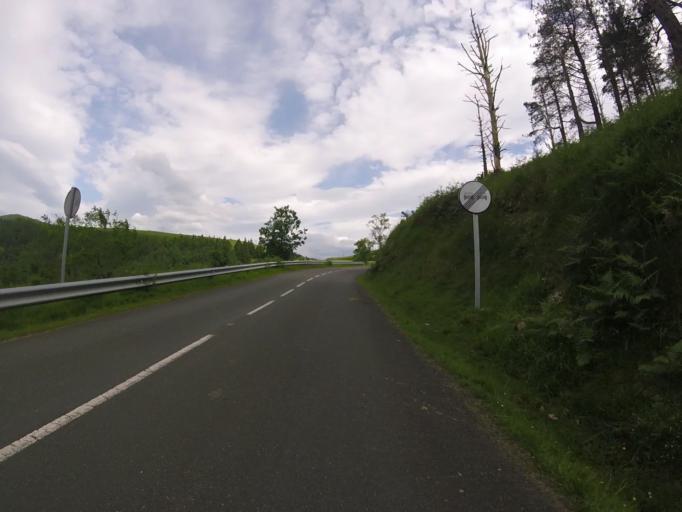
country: ES
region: Navarre
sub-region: Provincia de Navarra
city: Arano
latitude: 43.2440
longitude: -1.8430
